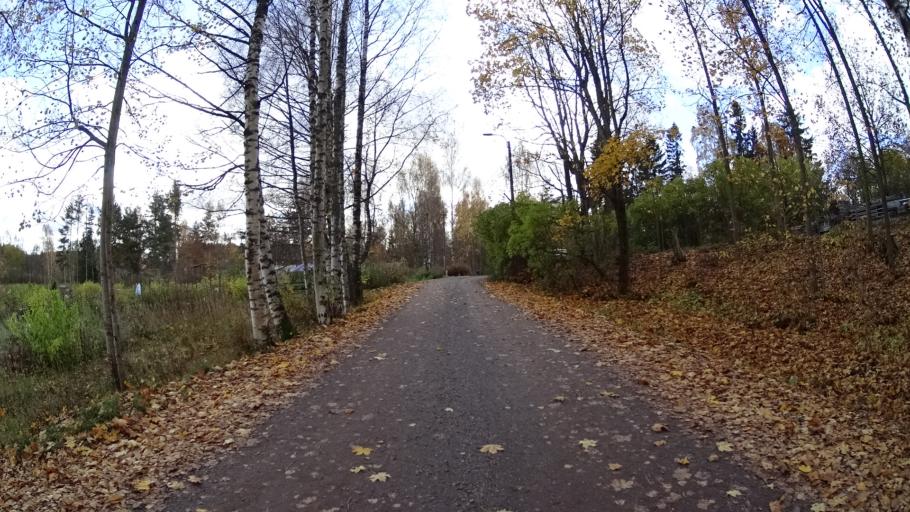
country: FI
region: Uusimaa
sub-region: Helsinki
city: Kilo
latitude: 60.2618
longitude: 24.7930
